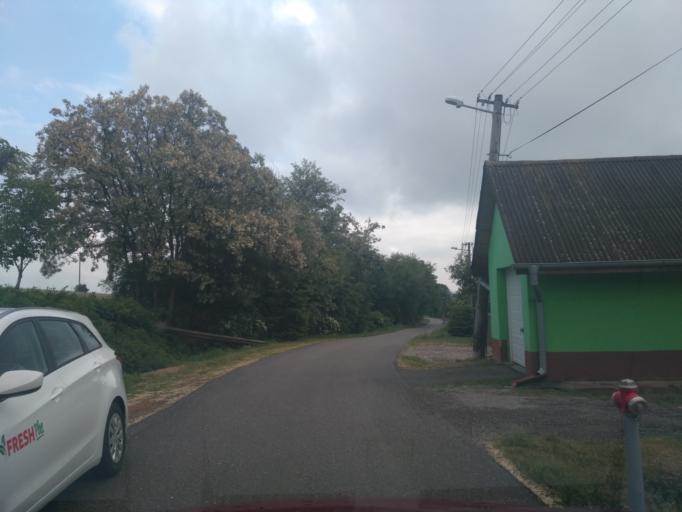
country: SK
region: Kosicky
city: Moldava nad Bodvou
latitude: 48.6886
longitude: 21.0746
